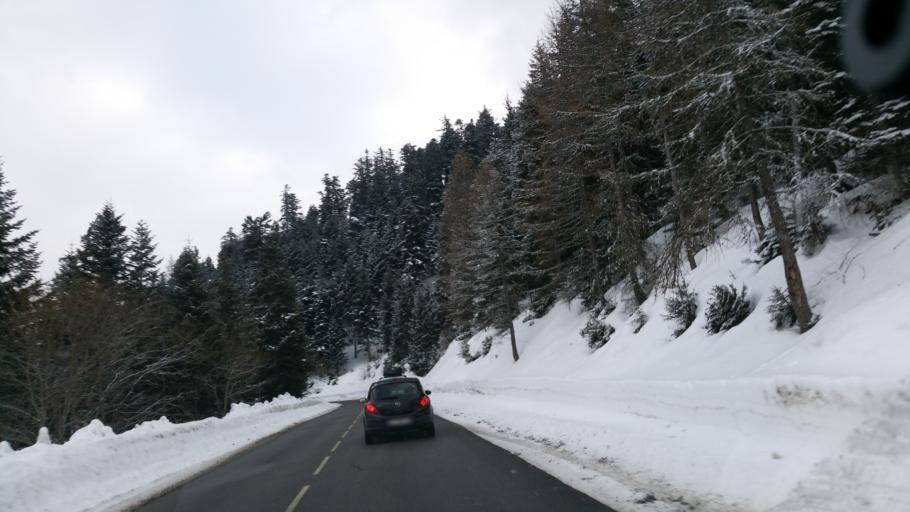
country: FR
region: Rhone-Alpes
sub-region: Departement de la Savoie
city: Villargondran
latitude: 45.2356
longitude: 6.3985
